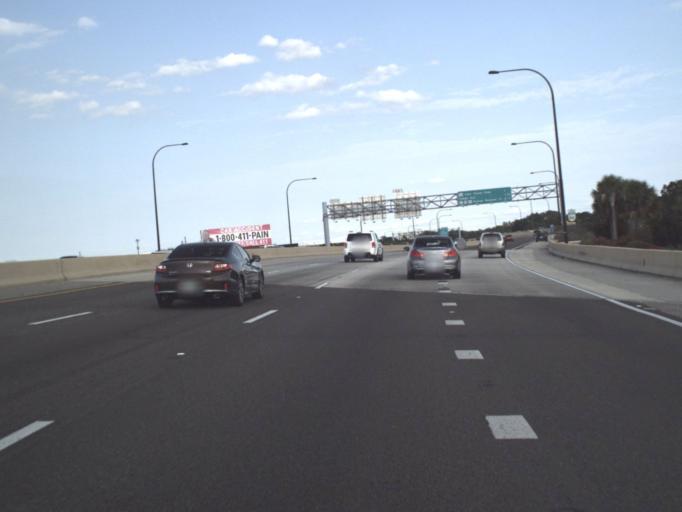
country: US
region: Florida
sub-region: Orange County
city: Pine Hills
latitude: 28.5479
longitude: -81.4345
